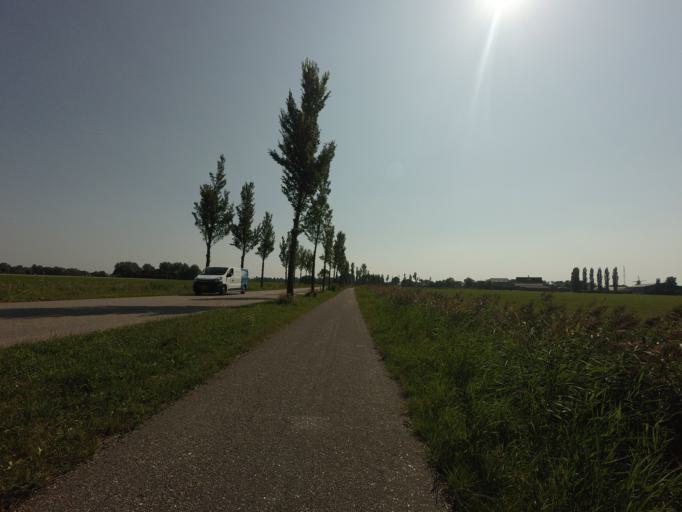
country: NL
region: Groningen
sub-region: Gemeente Zuidhorn
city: Grijpskerk
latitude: 53.2712
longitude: 6.3069
